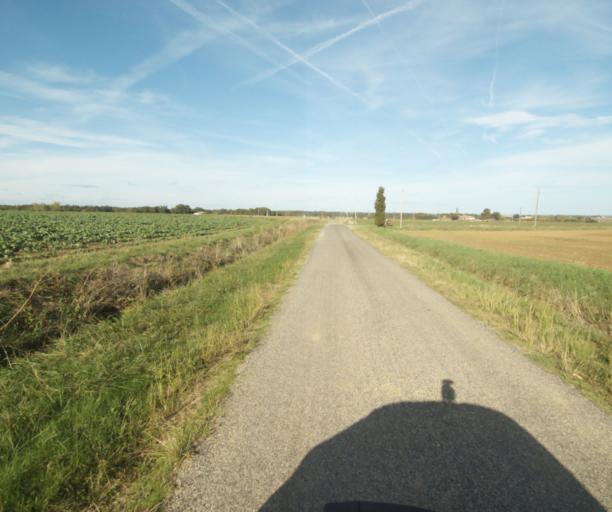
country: FR
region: Midi-Pyrenees
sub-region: Departement du Tarn-et-Garonne
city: Finhan
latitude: 43.9253
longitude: 1.1377
